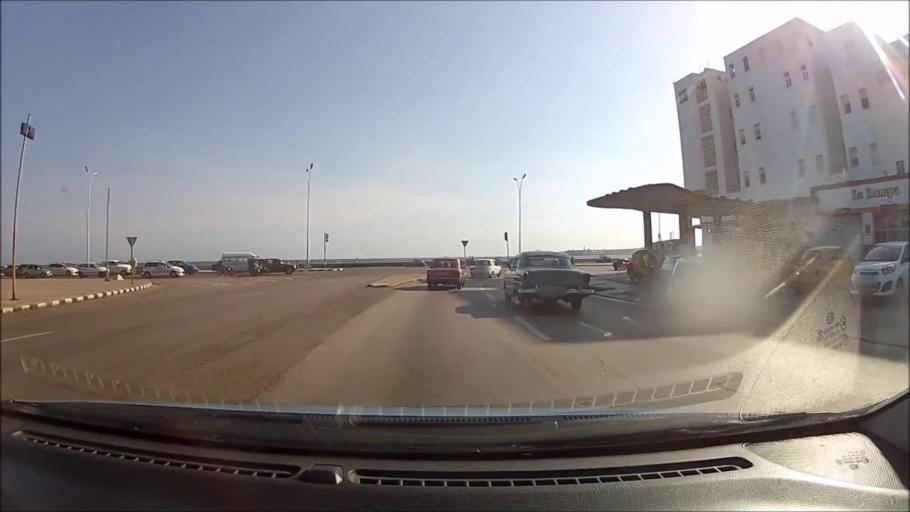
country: CU
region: La Habana
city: Havana
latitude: 23.1402
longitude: -82.3826
